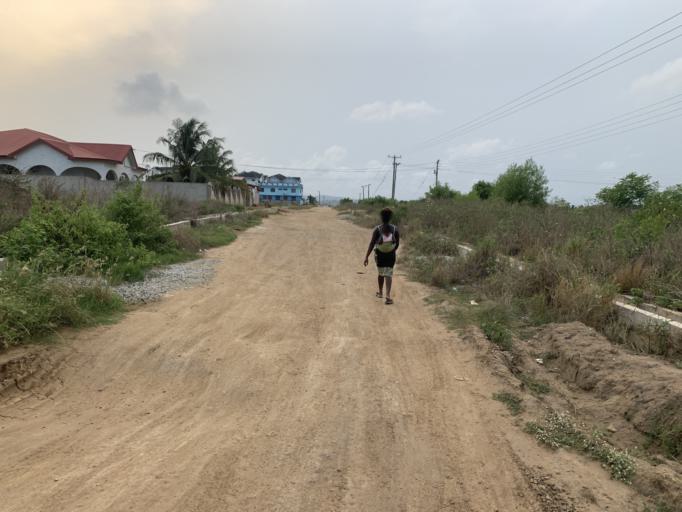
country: GH
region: Central
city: Winneba
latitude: 5.3821
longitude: -0.6248
